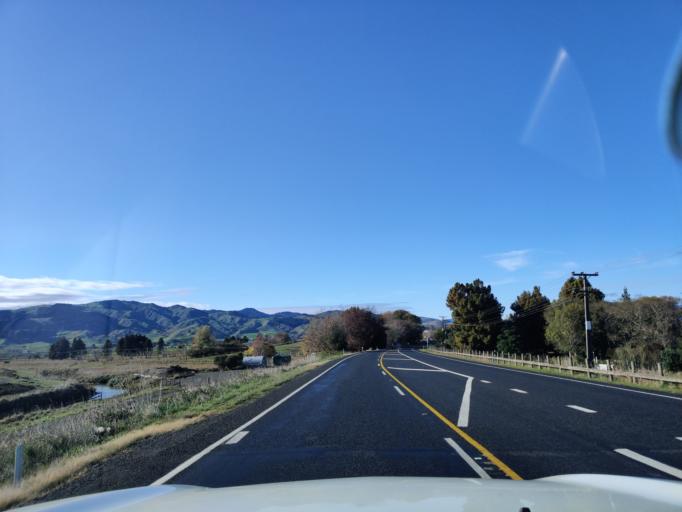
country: NZ
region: Waikato
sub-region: Hauraki District
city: Paeroa
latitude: -37.3583
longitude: 175.6514
